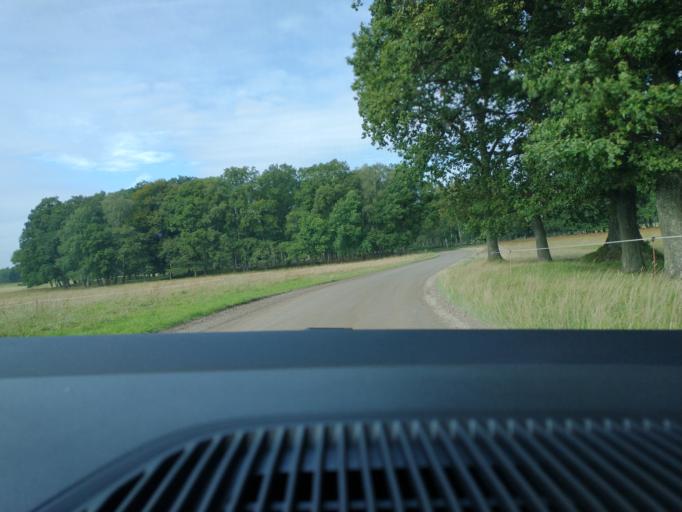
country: SE
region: Skane
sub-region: Lunds Kommun
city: Veberod
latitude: 55.6699
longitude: 13.4550
